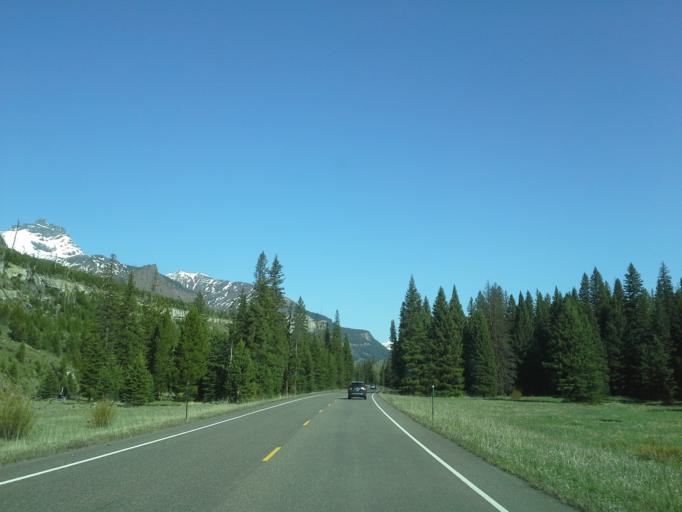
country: US
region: Montana
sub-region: Carbon County
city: Red Lodge
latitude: 44.9642
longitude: -109.8228
